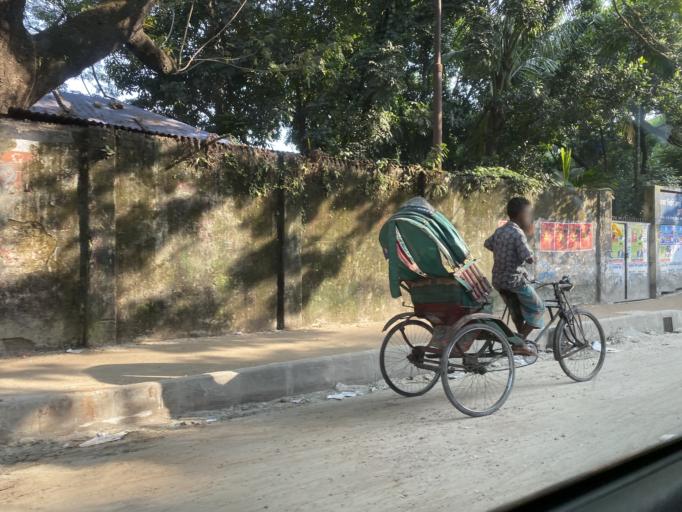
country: BD
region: Dhaka
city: Azimpur
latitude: 23.7335
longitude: 90.3874
